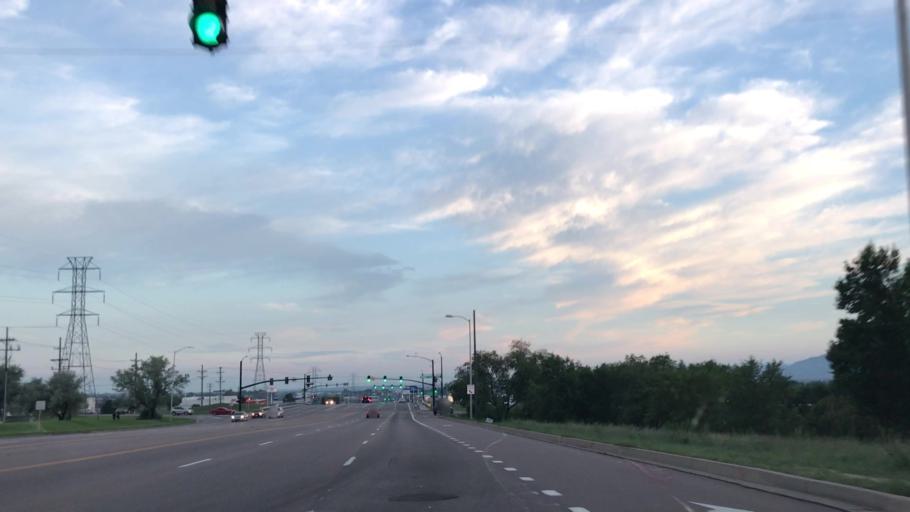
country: US
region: Colorado
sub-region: El Paso County
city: Cimarron Hills
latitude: 38.8419
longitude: -104.7576
